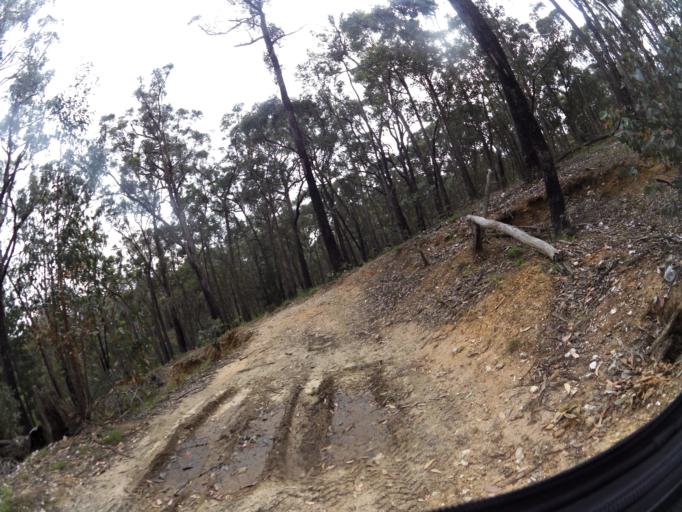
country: AU
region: Victoria
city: Brown Hill
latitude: -37.4896
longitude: 143.9068
